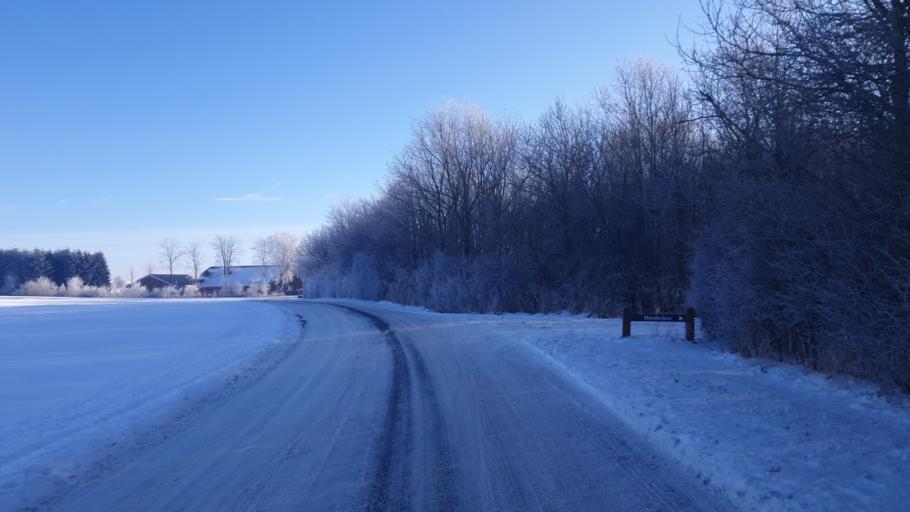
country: DK
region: Central Jutland
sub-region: Hedensted Kommune
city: Hedensted
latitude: 55.8054
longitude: 9.7219
